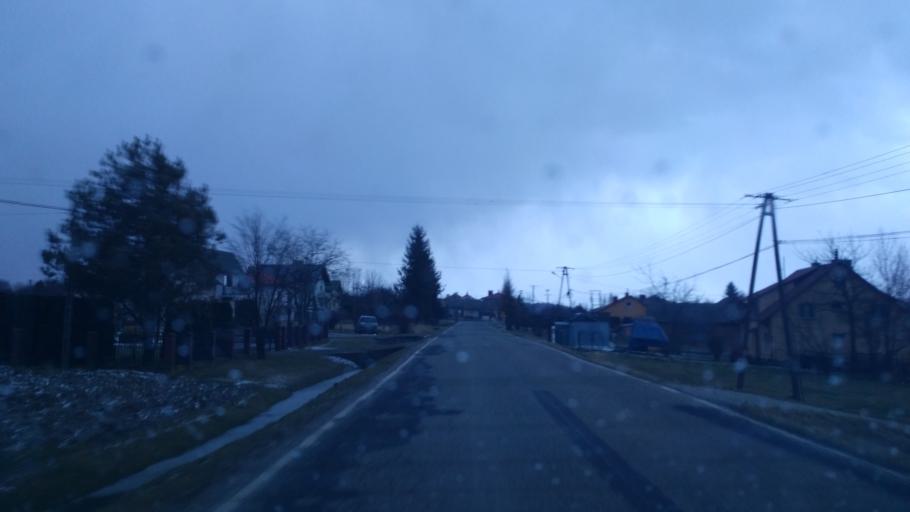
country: PL
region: Subcarpathian Voivodeship
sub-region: Powiat rzeszowski
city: Hyzne
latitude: 49.9249
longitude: 22.1948
